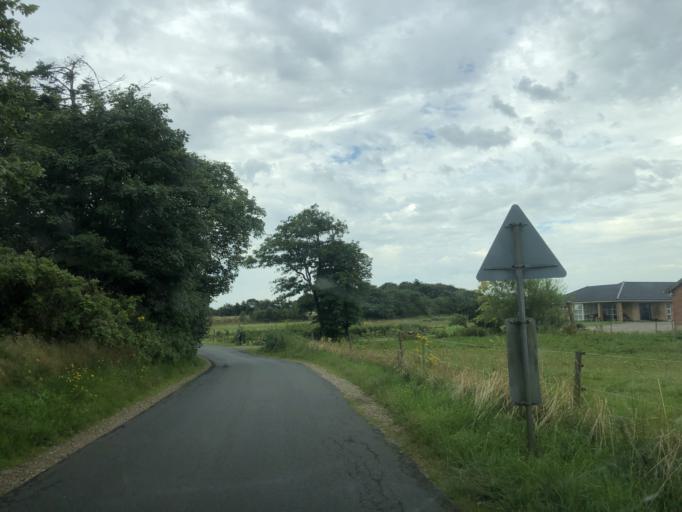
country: DK
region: Central Jutland
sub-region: Holstebro Kommune
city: Holstebro
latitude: 56.3739
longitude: 8.5174
